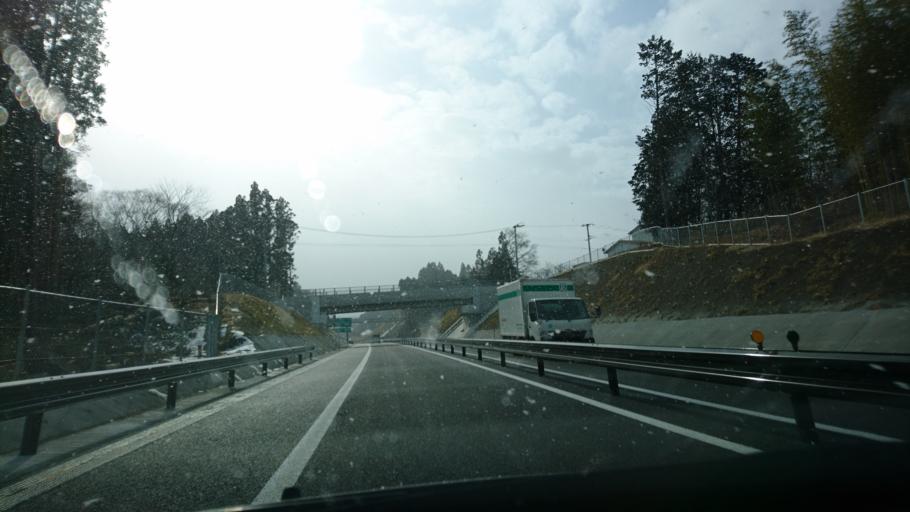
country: JP
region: Iwate
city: Ofunato
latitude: 38.8080
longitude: 141.5442
